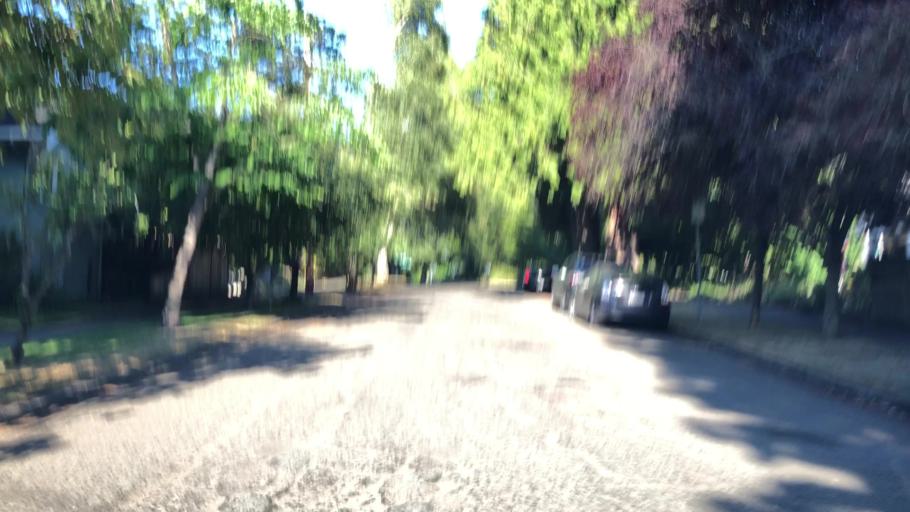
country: US
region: Washington
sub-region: King County
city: Seattle
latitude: 47.6748
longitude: -122.3109
